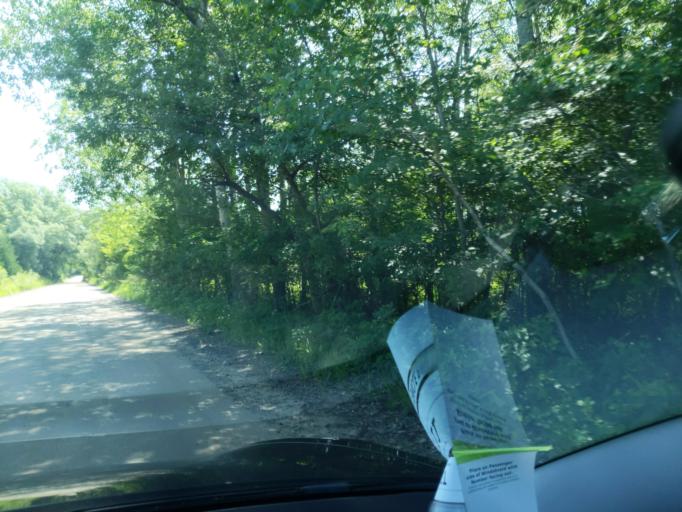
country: US
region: Michigan
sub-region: Cheboygan County
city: Cheboygan
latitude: 45.6501
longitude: -84.6247
